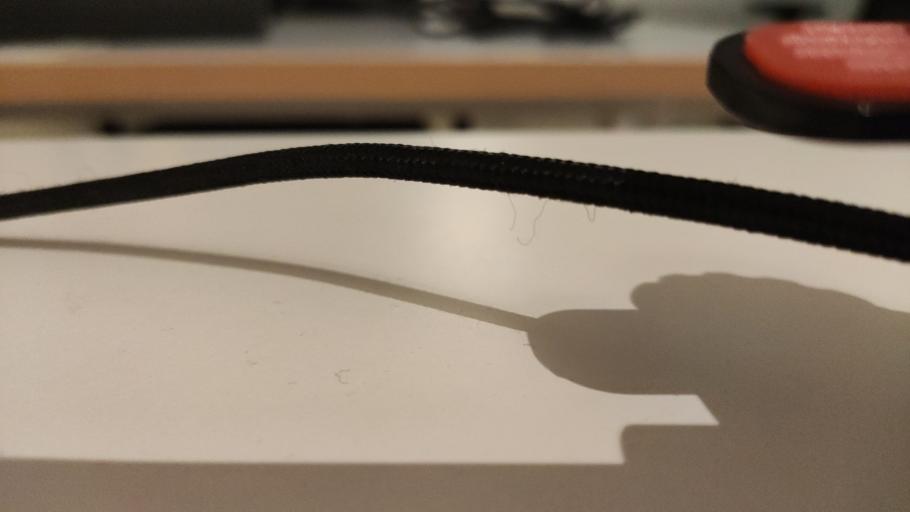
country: RU
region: Moskovskaya
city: Kurovskoye
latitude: 55.6055
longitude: 38.9272
